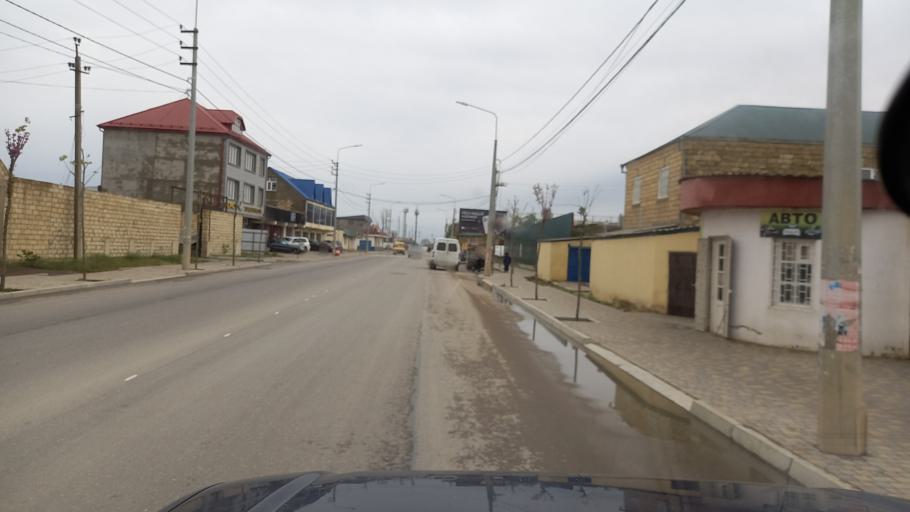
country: RU
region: Dagestan
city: Derbent
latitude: 42.0806
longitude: 48.2956
